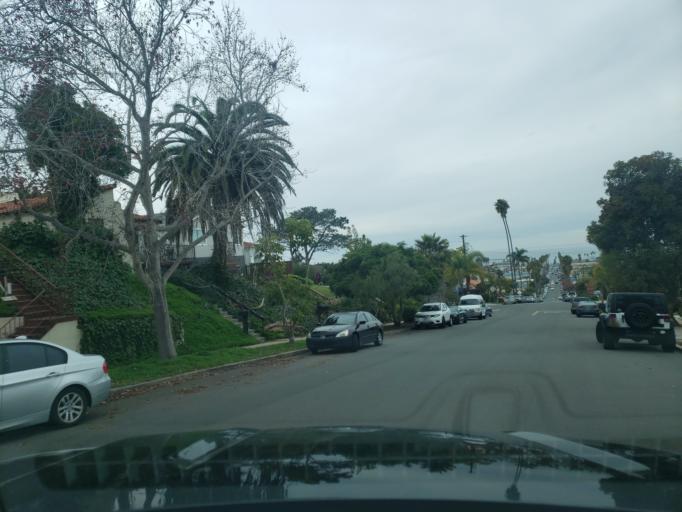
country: US
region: California
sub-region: San Diego County
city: Coronado
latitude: 32.7422
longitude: -117.2434
